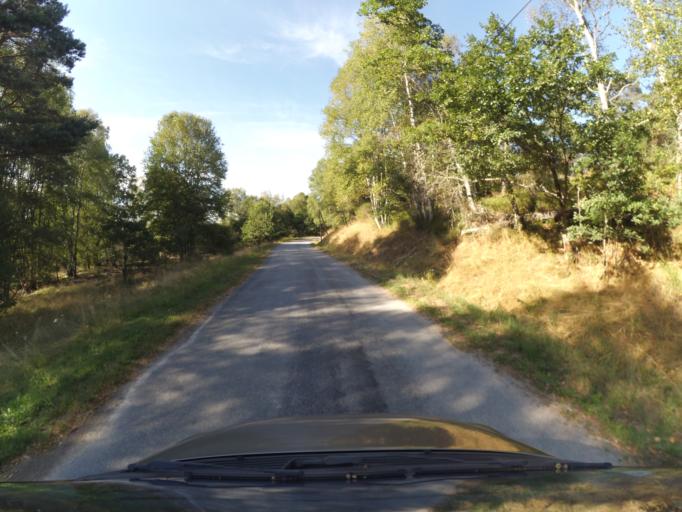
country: FR
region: Limousin
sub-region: Departement de la Correze
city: Bugeat
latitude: 45.6974
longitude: 1.9970
